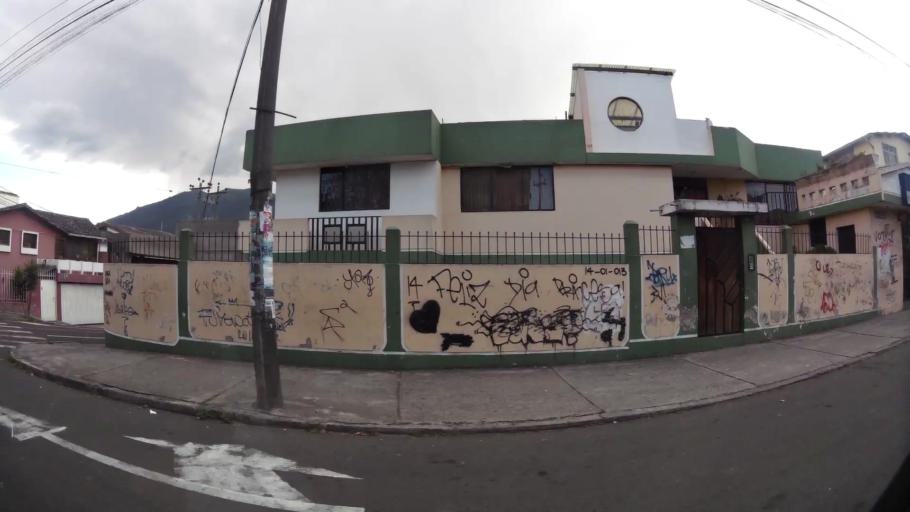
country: EC
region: Pichincha
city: Quito
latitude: -0.1331
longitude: -78.4870
